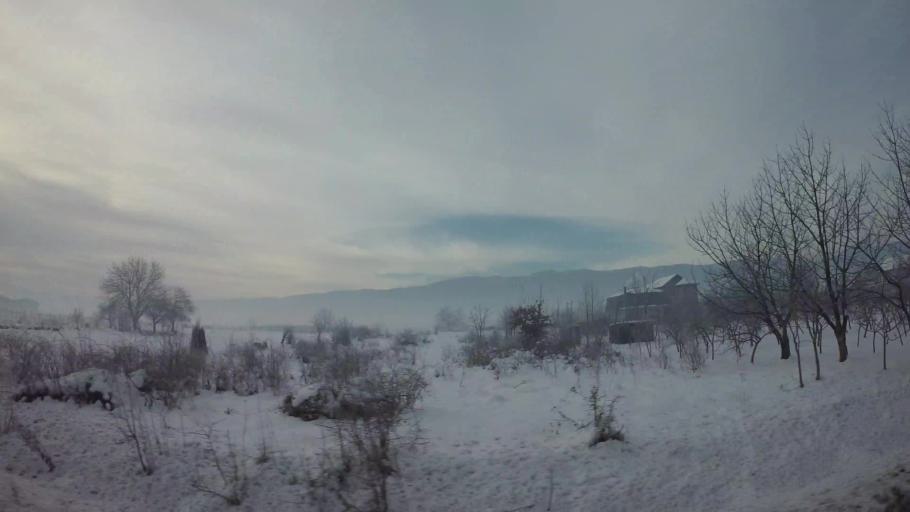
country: BA
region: Federation of Bosnia and Herzegovina
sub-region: Kanton Sarajevo
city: Sarajevo
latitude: 43.8252
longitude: 18.3436
